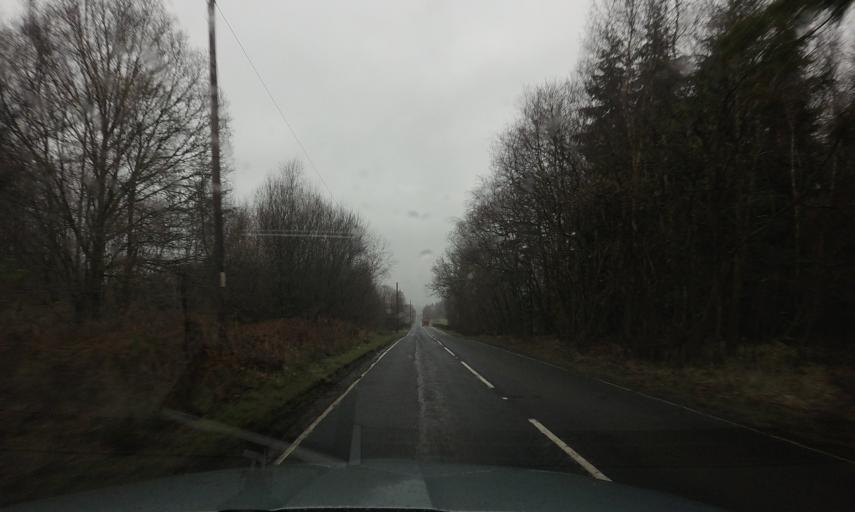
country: GB
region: Scotland
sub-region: Stirling
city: Balfron
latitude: 56.1146
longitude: -4.3589
